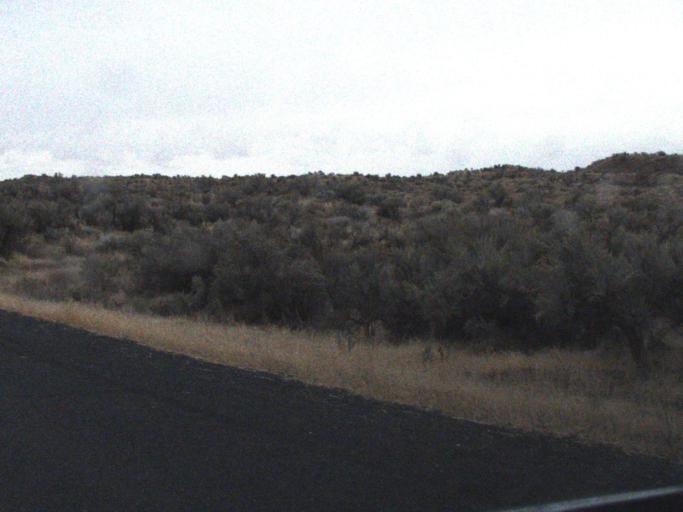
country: US
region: Washington
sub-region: Adams County
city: Ritzville
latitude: 46.7953
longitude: -118.5128
